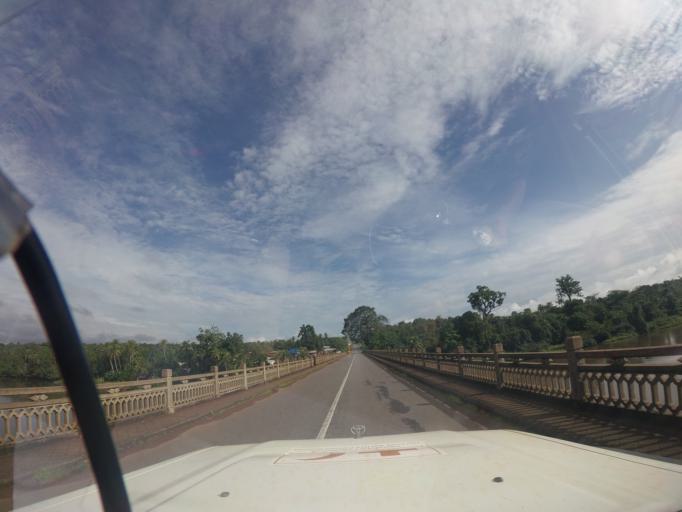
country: SL
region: Northern Province
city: Kambia
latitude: 9.1191
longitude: -12.9316
